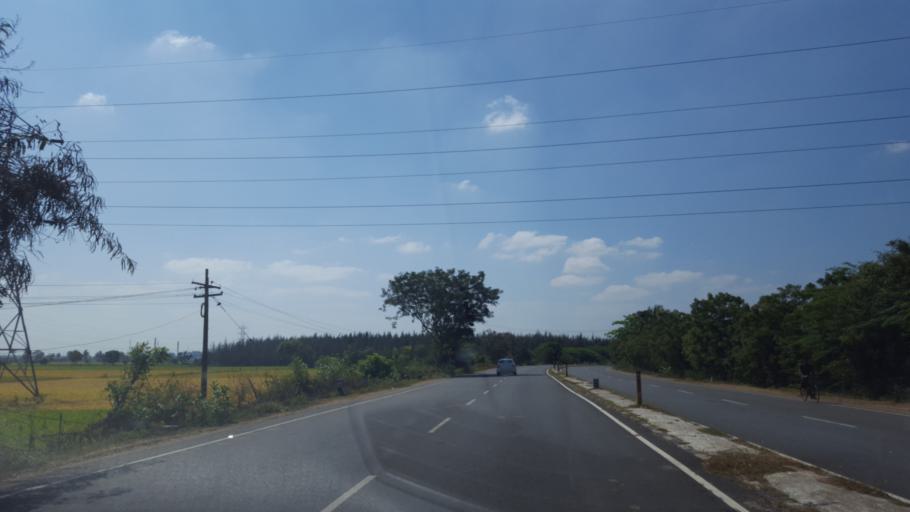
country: IN
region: Tamil Nadu
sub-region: Kancheepuram
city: Mamallapuram
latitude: 12.7104
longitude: 80.1861
